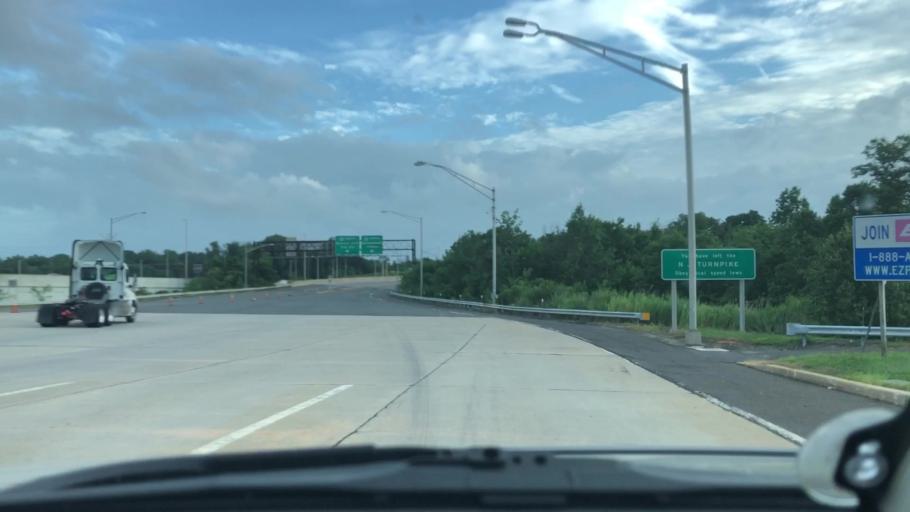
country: US
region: New Jersey
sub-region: Burlington County
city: Bordentown
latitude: 40.1257
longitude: -74.7010
